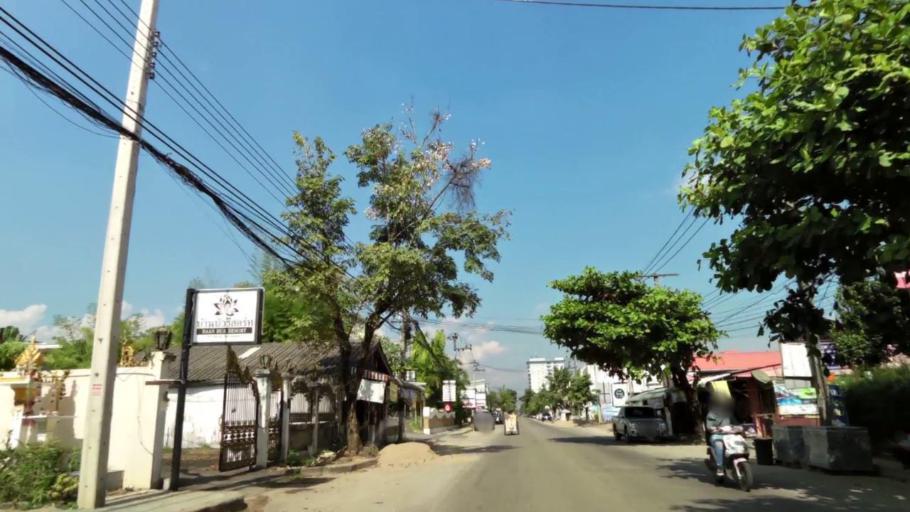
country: TH
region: Chiang Rai
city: Chiang Rai
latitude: 19.8951
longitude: 99.8275
